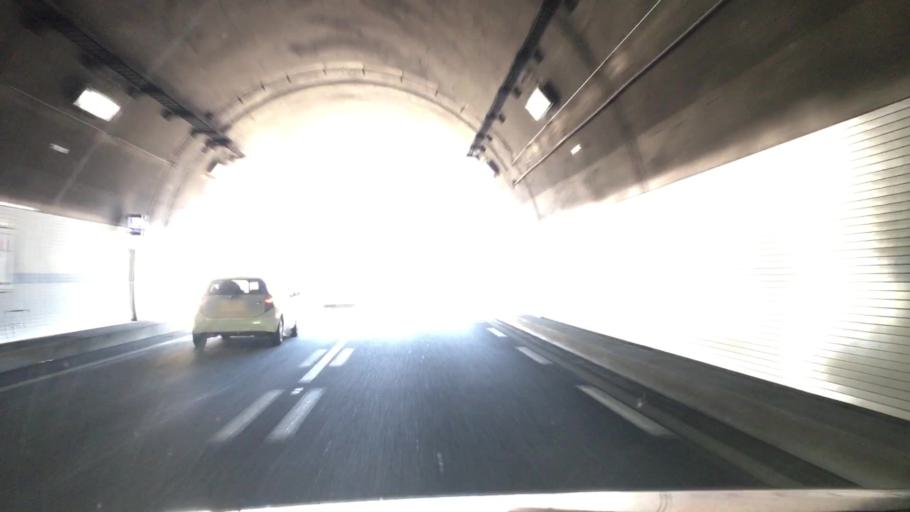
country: JP
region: Nagano
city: Nagano-shi
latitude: 36.5171
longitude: 138.1569
